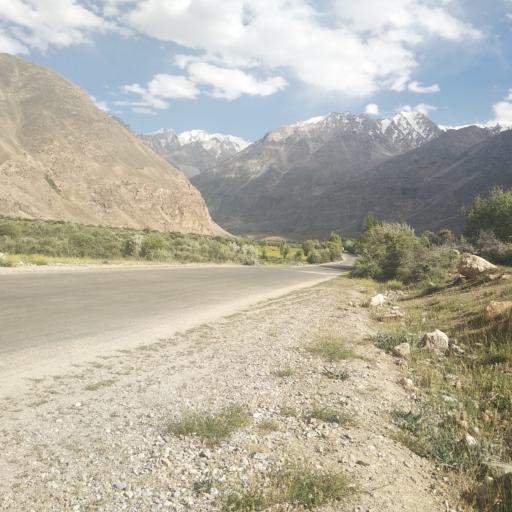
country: TJ
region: Gorno-Badakhshan
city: Roshtqal'a
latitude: 37.7285
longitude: 72.1593
